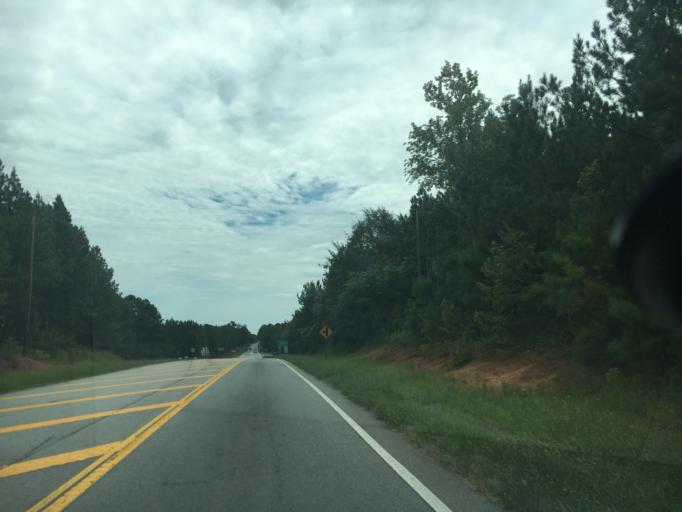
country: US
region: South Carolina
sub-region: Greenville County
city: Fountain Inn
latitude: 34.6411
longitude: -82.1478
